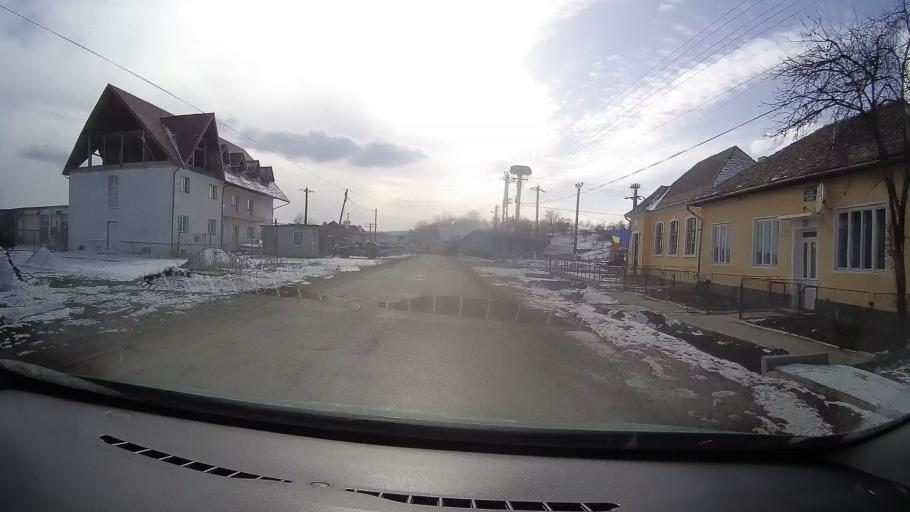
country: RO
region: Sibiu
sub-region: Comuna Bradeni
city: Bradeni
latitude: 46.0575
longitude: 24.7859
